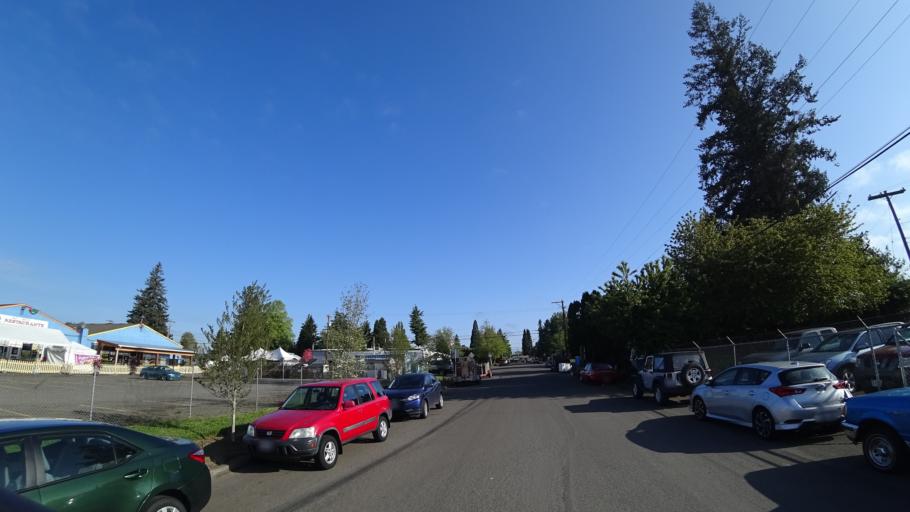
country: US
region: Oregon
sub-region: Washington County
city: Hillsboro
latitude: 45.5169
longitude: -122.9929
